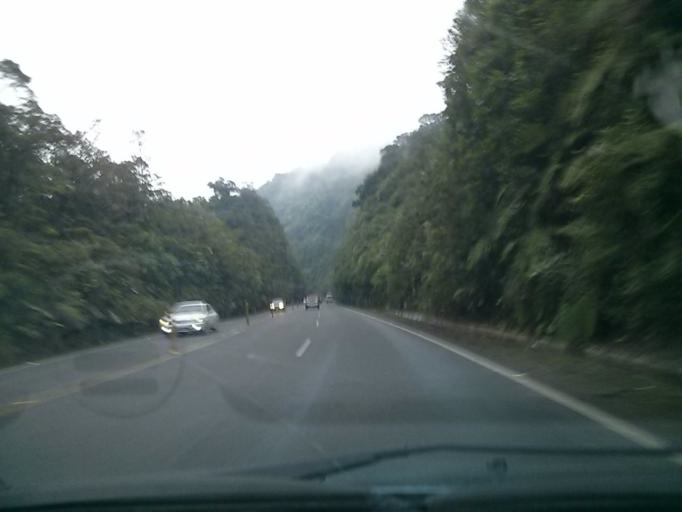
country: CR
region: Heredia
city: Angeles
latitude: 10.0557
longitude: -84.0135
